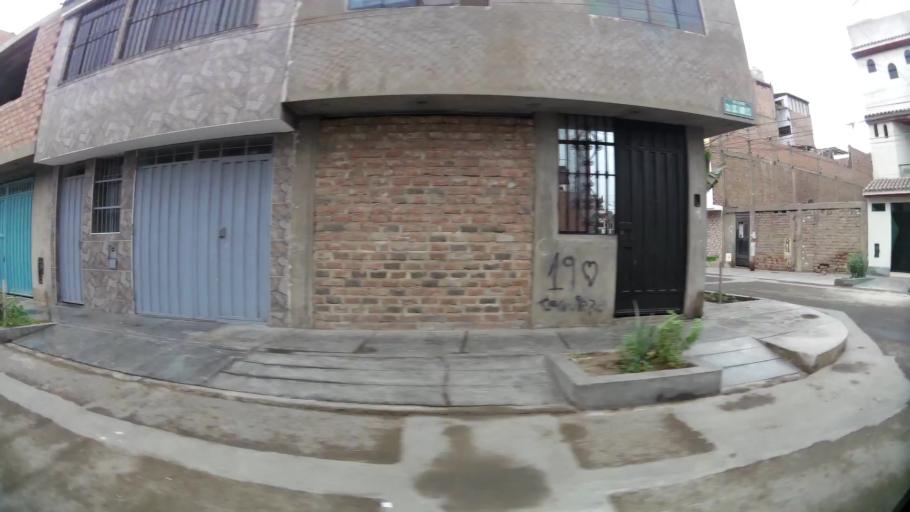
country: PE
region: Lima
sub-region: Lima
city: Independencia
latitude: -11.9757
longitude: -77.0736
